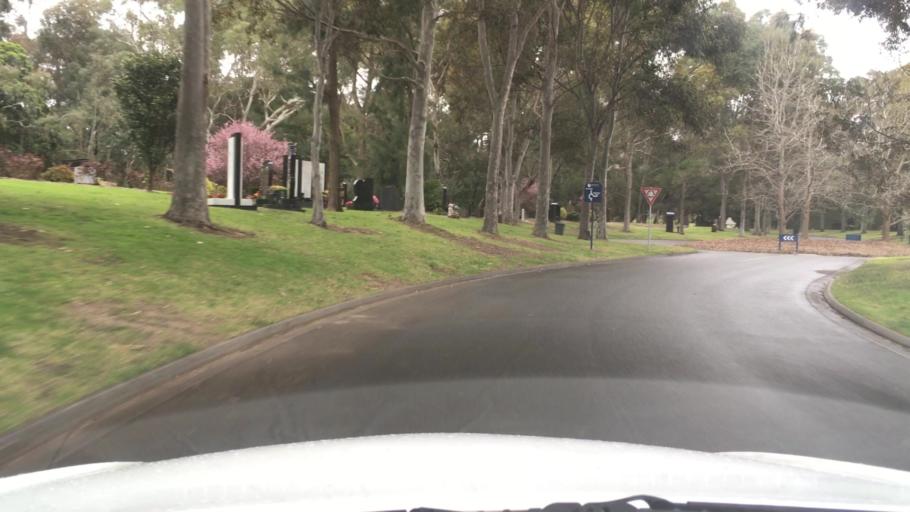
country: AU
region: Victoria
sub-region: Greater Dandenong
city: Noble Park North
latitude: -37.9467
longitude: 145.1799
